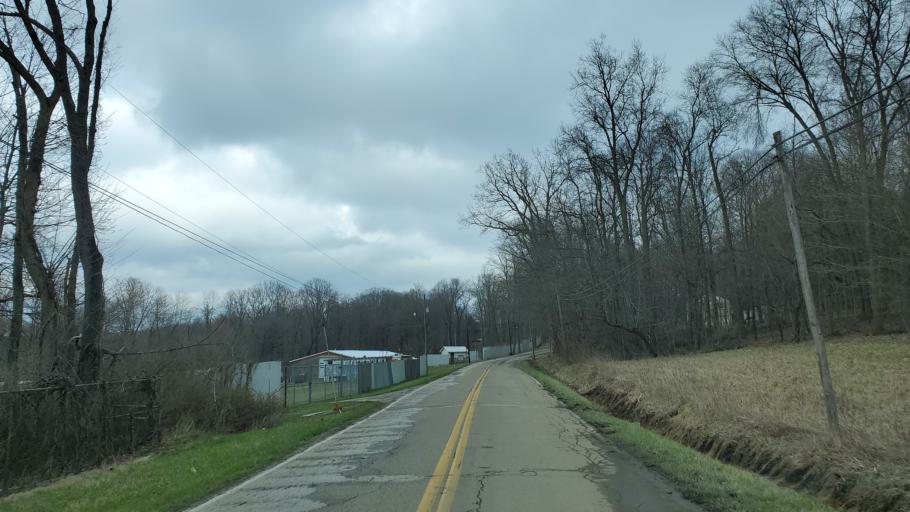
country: US
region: Ohio
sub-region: Licking County
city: Newark
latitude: 40.0396
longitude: -82.3786
